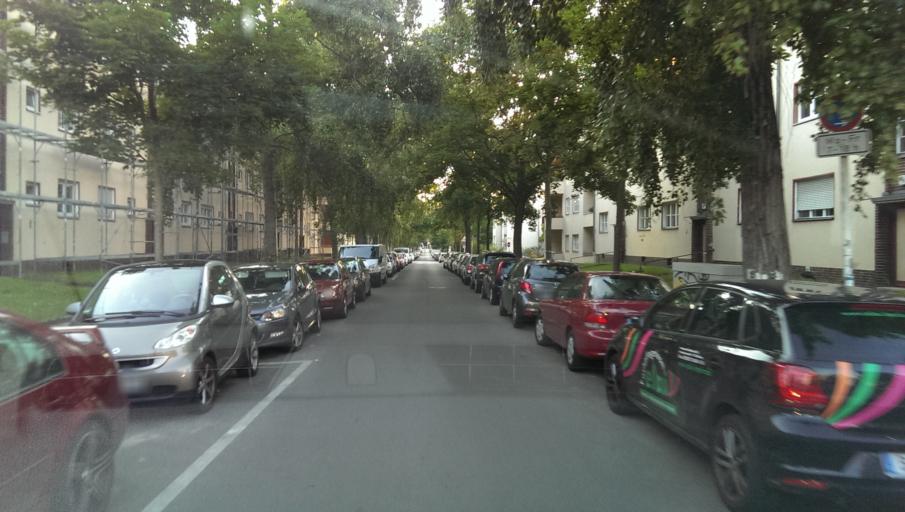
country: DE
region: Berlin
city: Lankwitz
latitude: 52.4291
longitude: 13.3415
